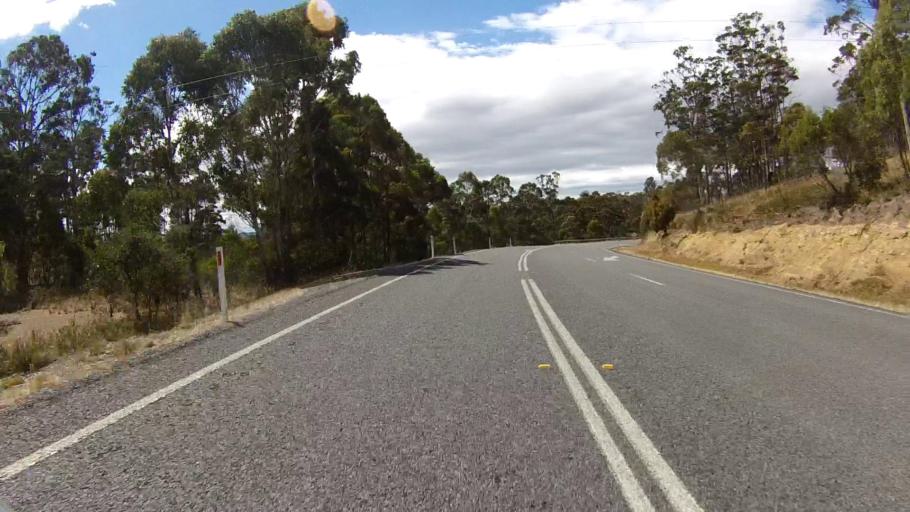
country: AU
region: Tasmania
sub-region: Sorell
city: Sorell
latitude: -42.6166
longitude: 147.6421
